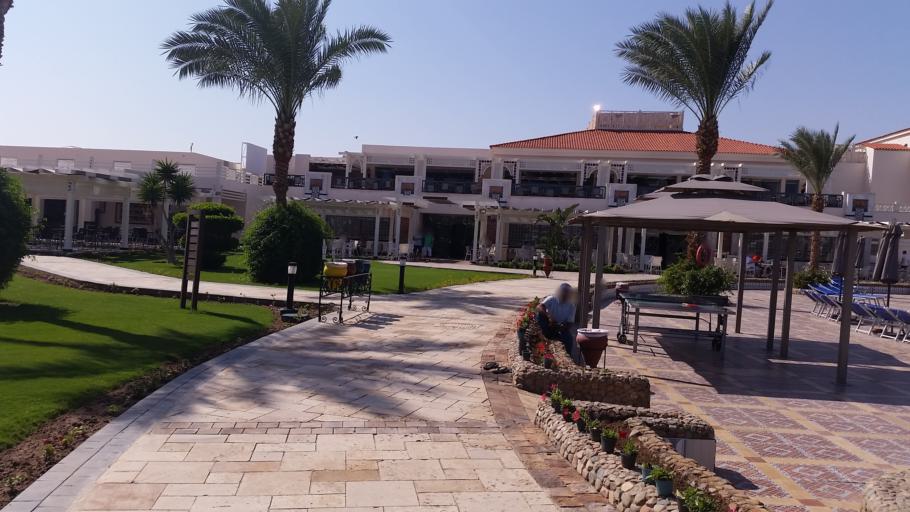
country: EG
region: Red Sea
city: Makadi Bay
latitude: 27.0974
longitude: 33.8326
